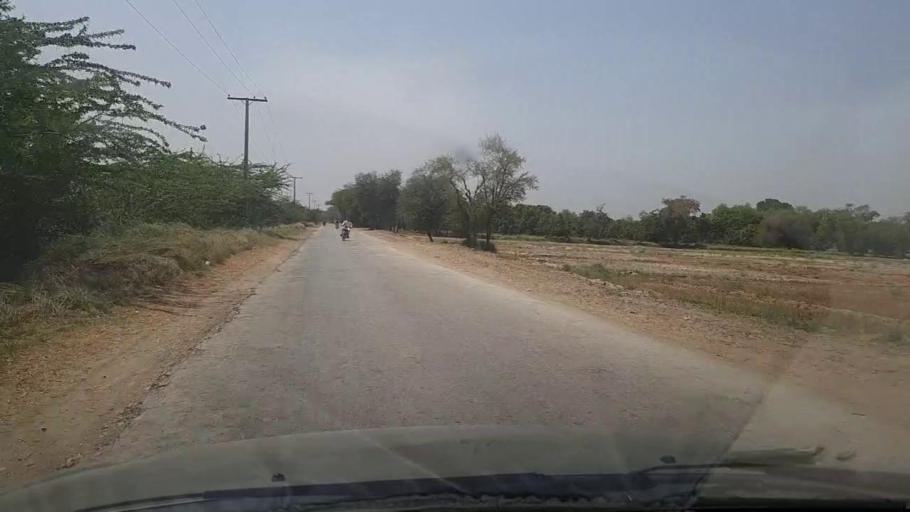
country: PK
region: Sindh
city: Bhiria
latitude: 26.8983
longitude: 68.2229
